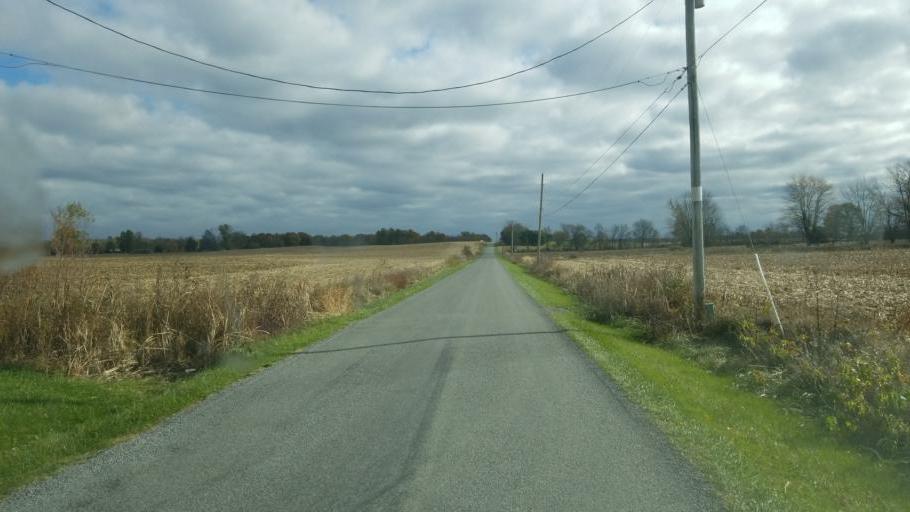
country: US
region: Ohio
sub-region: Crawford County
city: Galion
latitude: 40.6685
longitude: -82.7751
